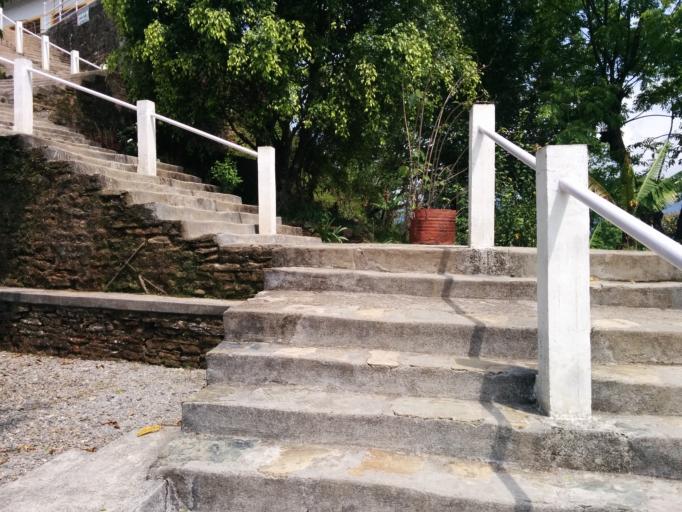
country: NP
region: Western Region
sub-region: Gandaki Zone
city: Pokhara
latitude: 28.2006
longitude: 83.9465
